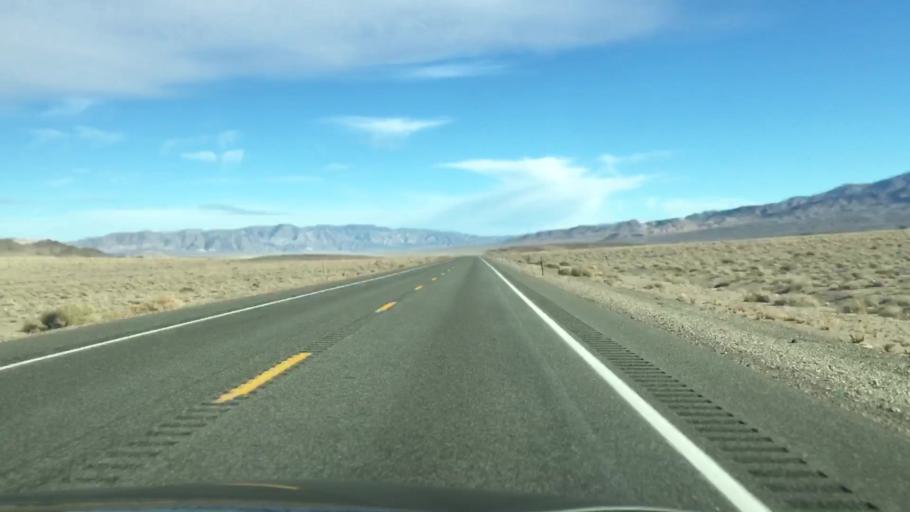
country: US
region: Nevada
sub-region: Mineral County
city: Hawthorne
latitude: 38.5489
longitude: -118.4321
